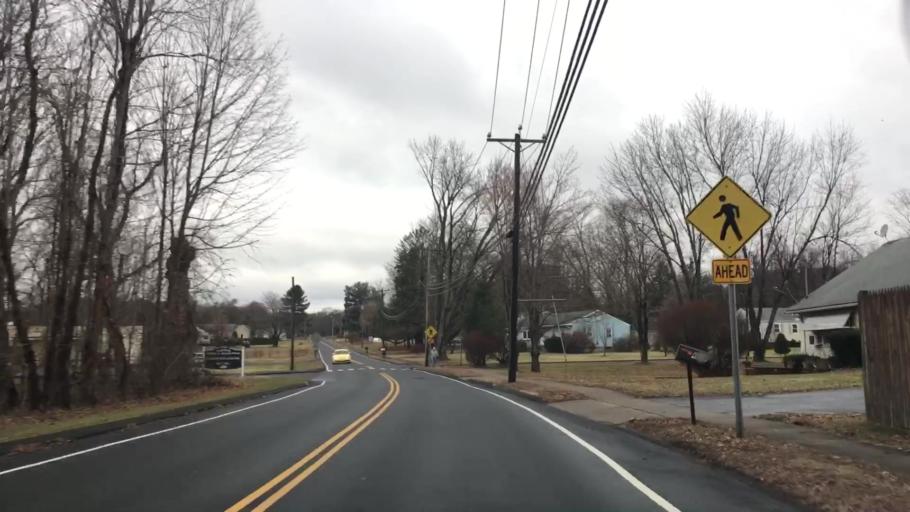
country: US
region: Connecticut
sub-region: Tolland County
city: Rockville
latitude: 41.8511
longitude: -72.4928
